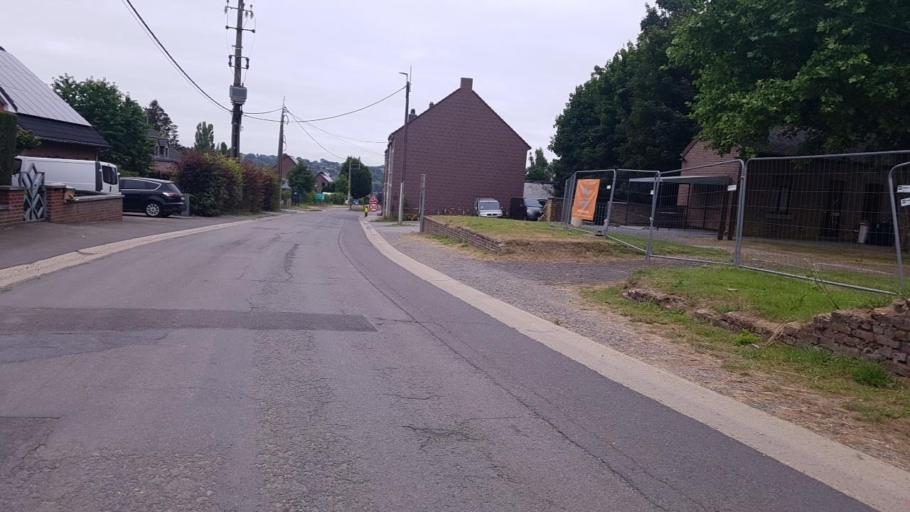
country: BE
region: Wallonia
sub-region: Province de Liege
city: Soumagne
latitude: 50.6196
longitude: 5.7383
